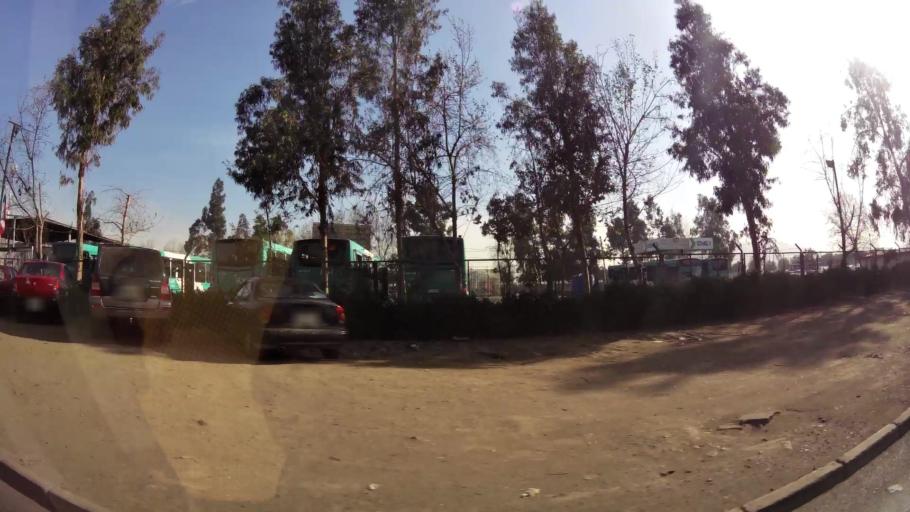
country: CL
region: Santiago Metropolitan
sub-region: Provincia de Santiago
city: Lo Prado
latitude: -33.4137
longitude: -70.7580
